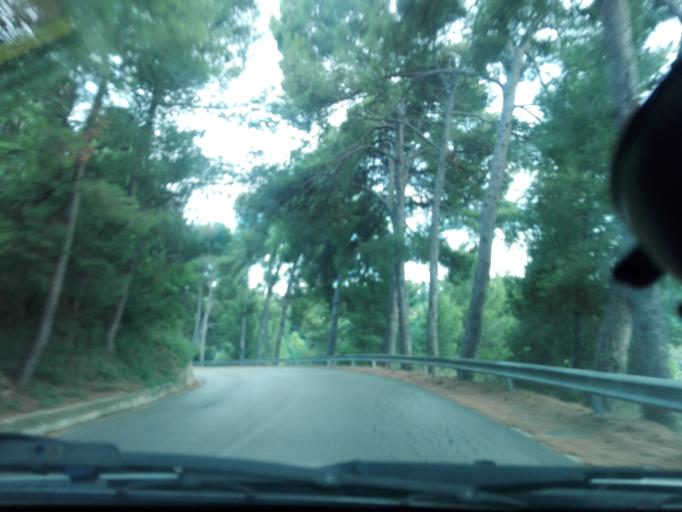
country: IT
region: Abruzzo
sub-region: Provincia di Pescara
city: Montesilvano Marina
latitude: 42.4948
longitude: 14.1438
